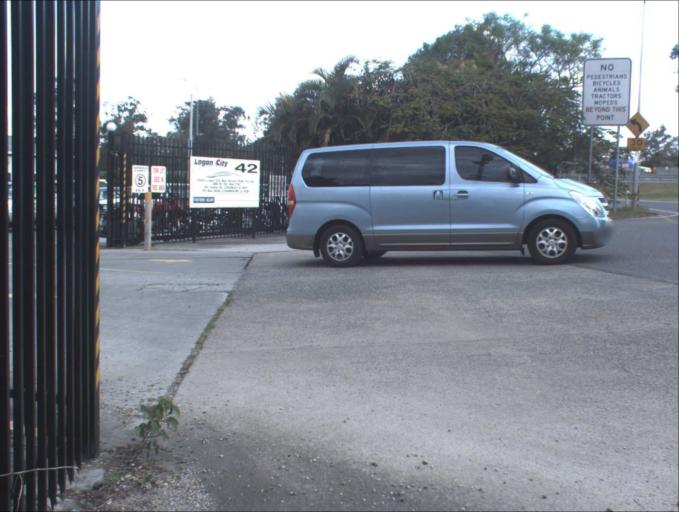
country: AU
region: Queensland
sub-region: Logan
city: Waterford West
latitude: -27.6672
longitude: 153.1249
